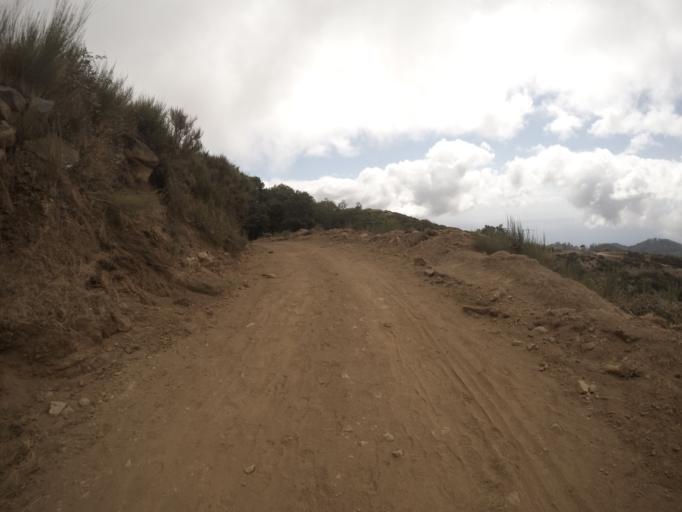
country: PT
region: Madeira
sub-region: Camara de Lobos
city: Curral das Freiras
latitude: 32.7132
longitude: -17.0090
